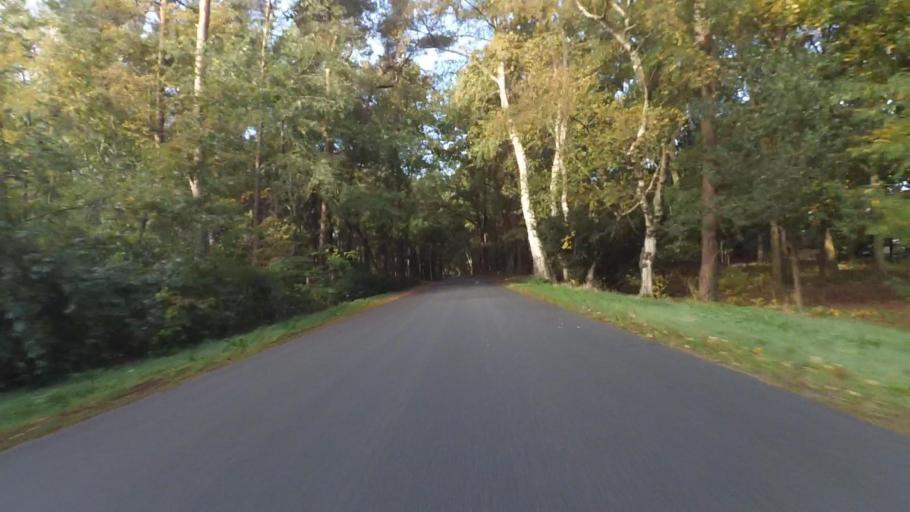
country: NL
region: Gelderland
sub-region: Gemeente Ermelo
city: Horst
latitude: 52.3206
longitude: 5.5891
